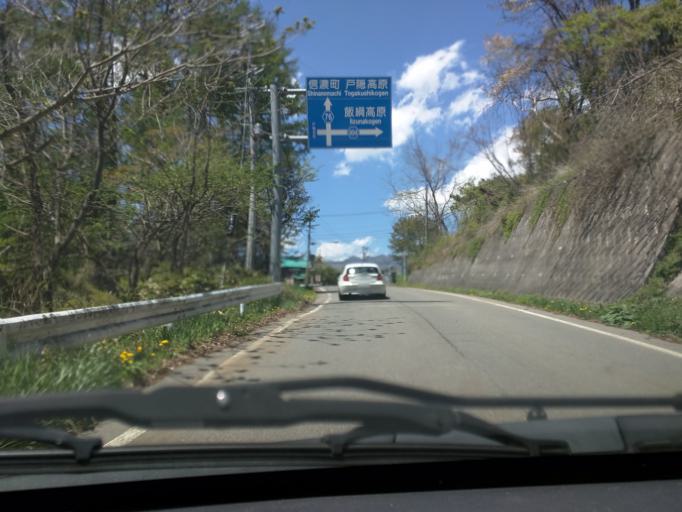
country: JP
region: Nagano
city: Nagano-shi
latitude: 36.6924
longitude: 138.1079
